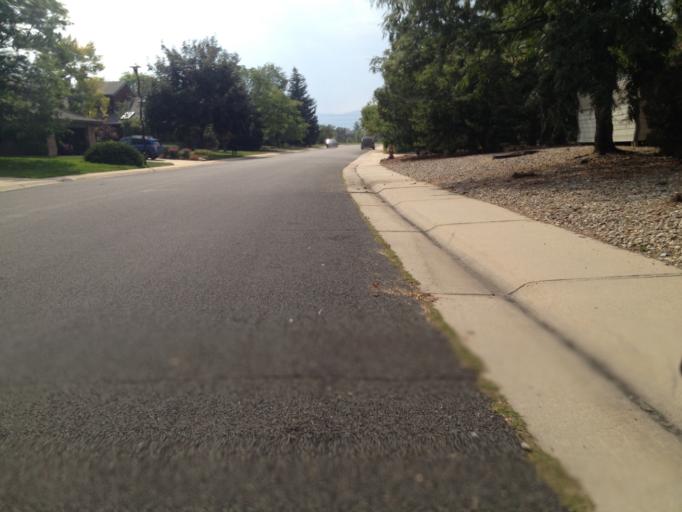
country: US
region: Colorado
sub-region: Boulder County
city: Louisville
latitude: 39.9888
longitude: -105.1519
